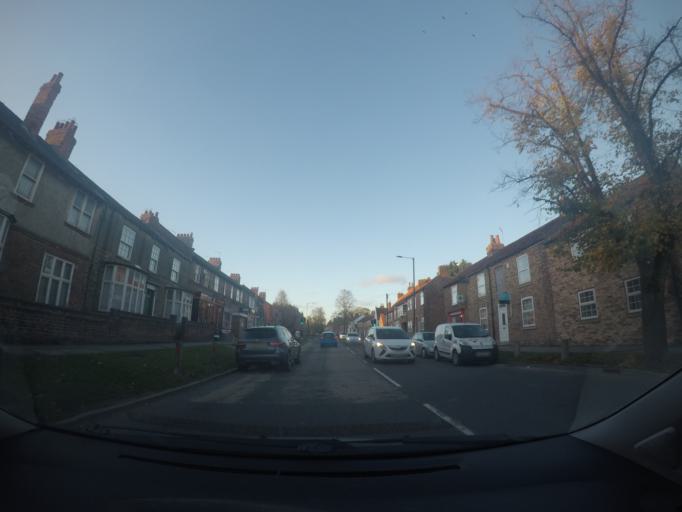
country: GB
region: England
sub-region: City of York
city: Fulford
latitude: 53.9338
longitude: -1.0712
